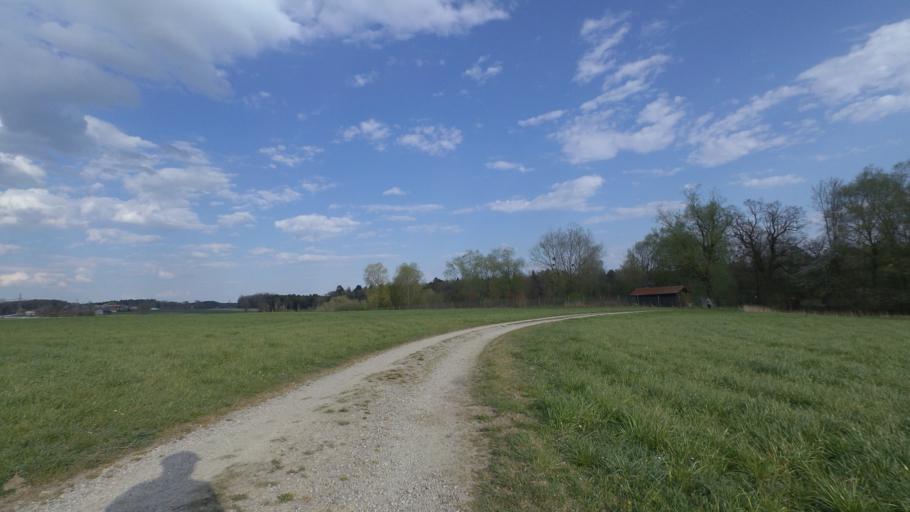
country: DE
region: Bavaria
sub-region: Upper Bavaria
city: Seeon-Seebruck
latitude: 47.9380
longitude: 12.4805
